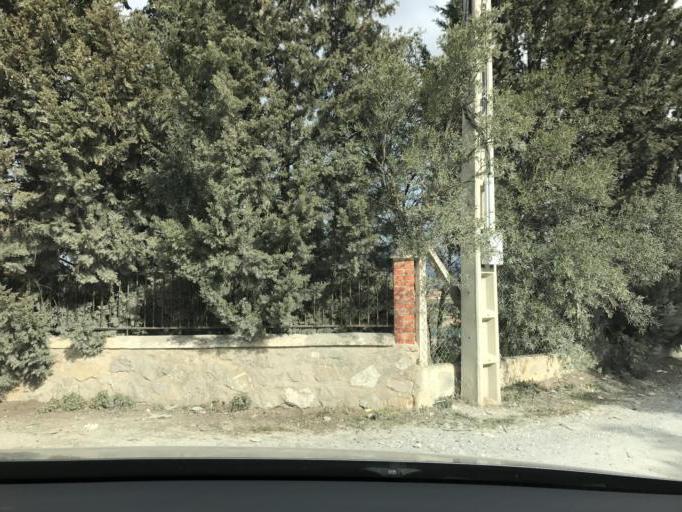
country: ES
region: Andalusia
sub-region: Provincia de Granada
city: Cullar-Vega
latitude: 37.1500
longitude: -3.6860
